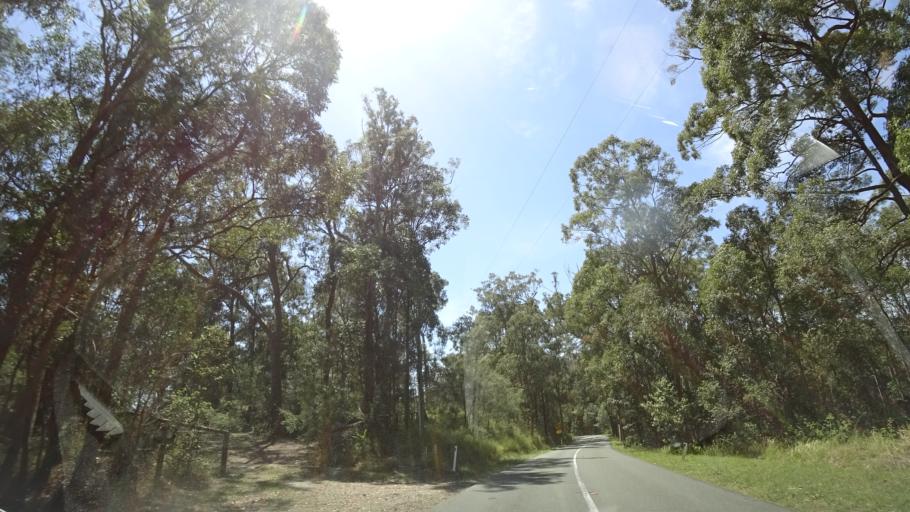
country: AU
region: Queensland
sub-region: Moreton Bay
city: Samford Valley
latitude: -27.4207
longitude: 152.8578
